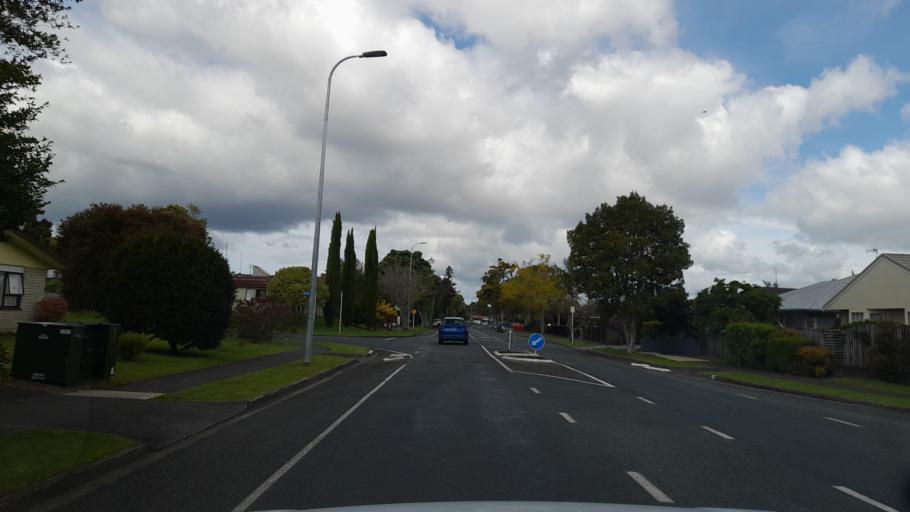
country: NZ
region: Northland
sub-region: Whangarei
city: Whangarei
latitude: -35.6911
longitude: 174.3012
